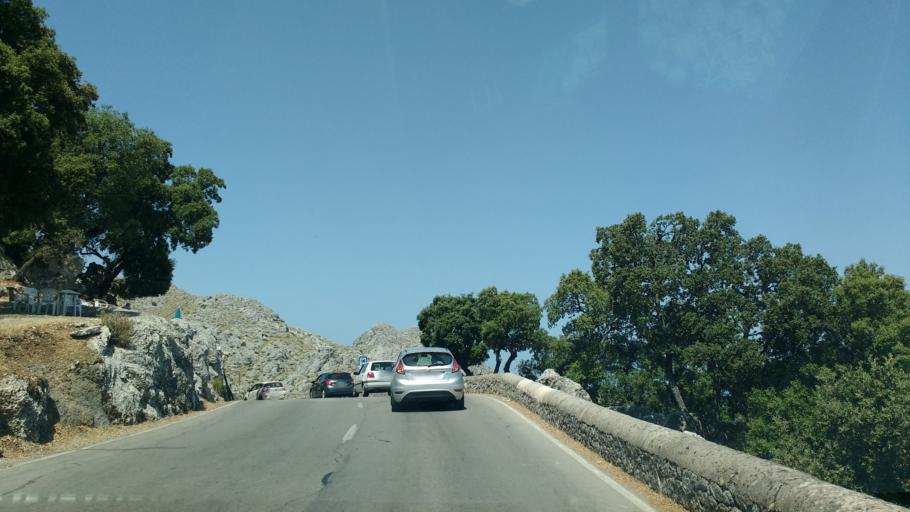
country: ES
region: Balearic Islands
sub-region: Illes Balears
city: Escorca
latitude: 39.8286
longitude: 2.8377
